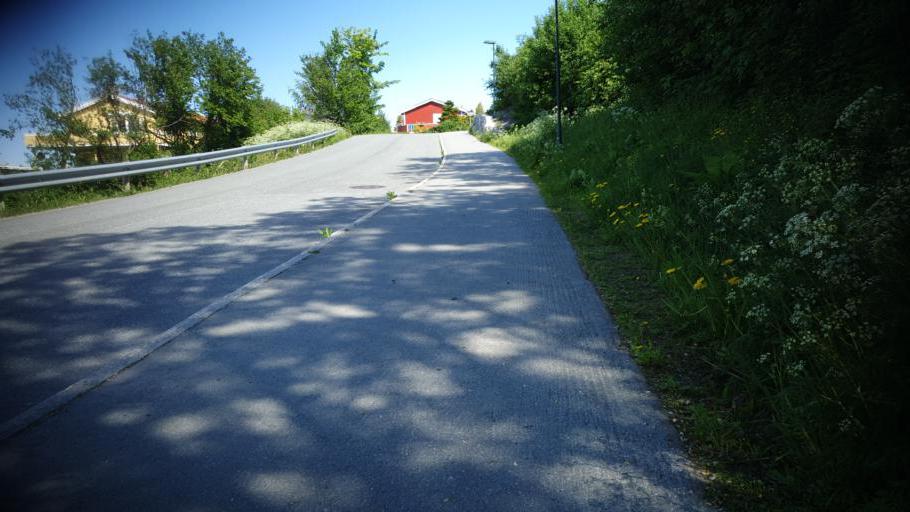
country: NO
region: Sor-Trondelag
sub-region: Malvik
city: Malvik
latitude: 63.4379
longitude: 10.6383
